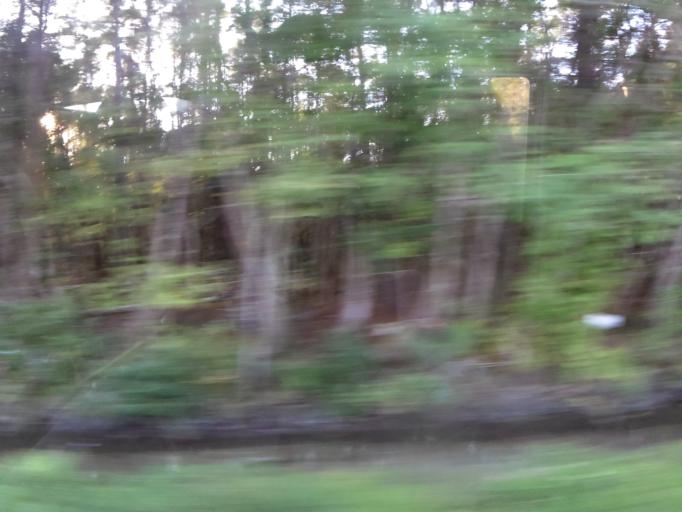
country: US
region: Florida
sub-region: Duval County
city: Jacksonville
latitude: 30.3478
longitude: -81.7646
